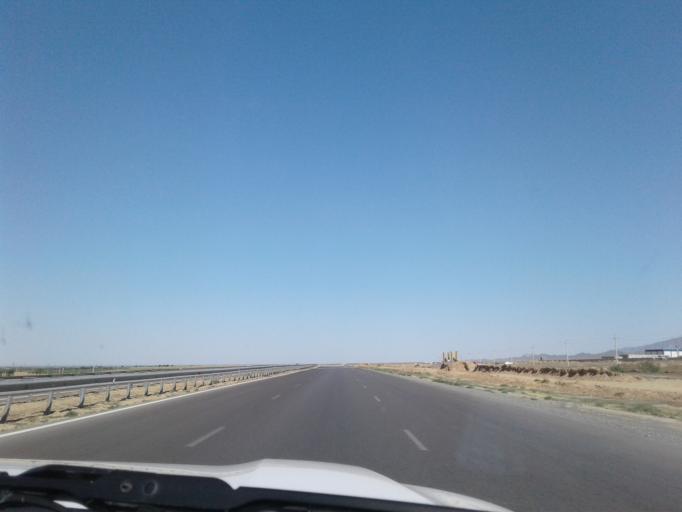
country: IR
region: Razavi Khorasan
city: Dargaz
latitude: 37.7665
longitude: 58.8990
